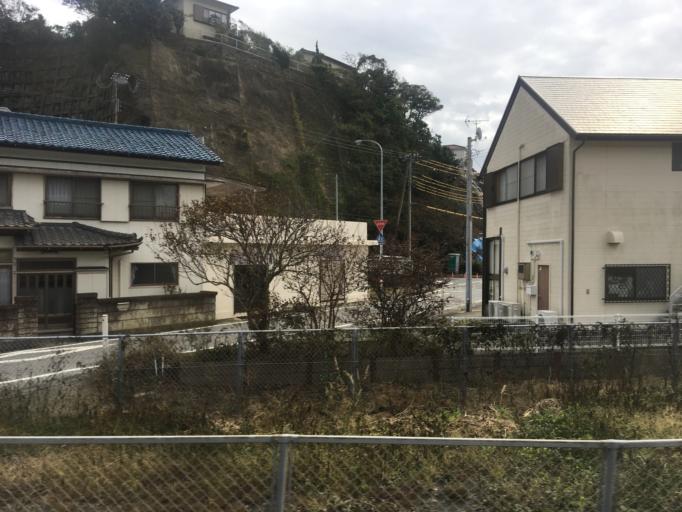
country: JP
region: Chiba
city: Katsuura
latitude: 35.1537
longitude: 140.3142
